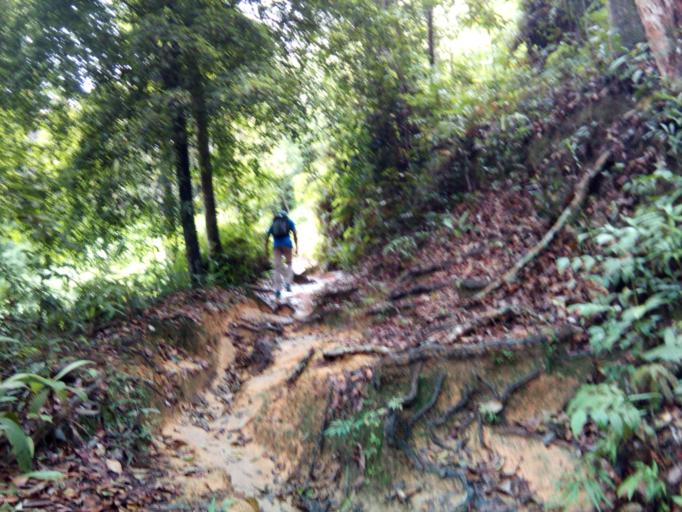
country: MY
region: Penang
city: Tanjung Tokong
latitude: 5.4287
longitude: 100.2894
